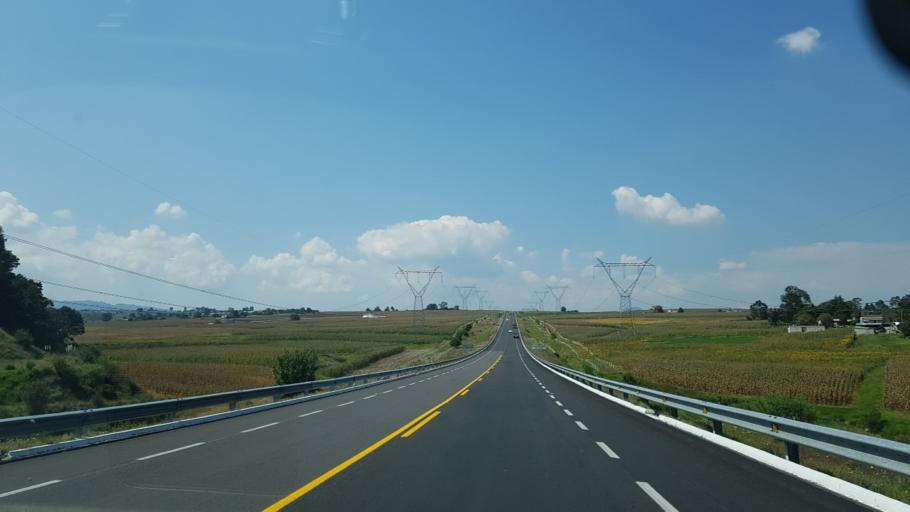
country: MX
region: Mexico
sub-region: Almoloya de Juarez
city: San Pedro de la Hortaliza (Ejido Almoloyan)
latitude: 19.3789
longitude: -99.8329
